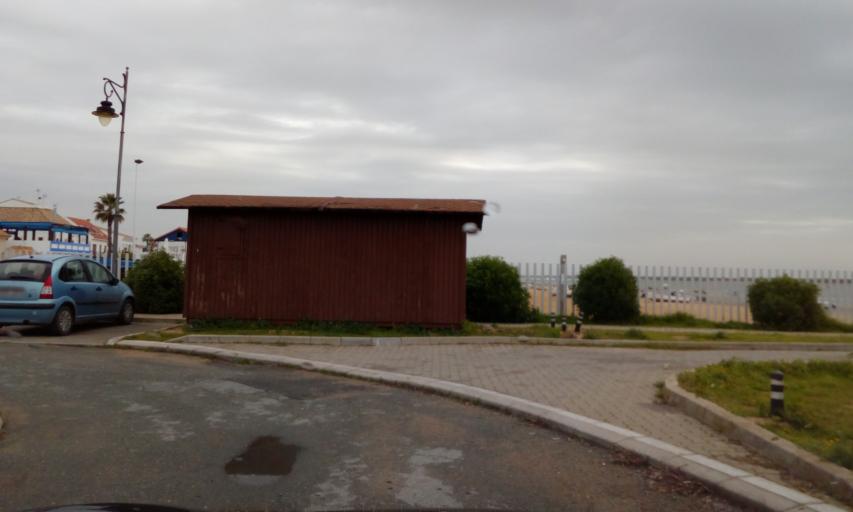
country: ES
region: Andalusia
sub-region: Provincia de Huelva
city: Cartaya
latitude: 37.2173
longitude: -7.1264
